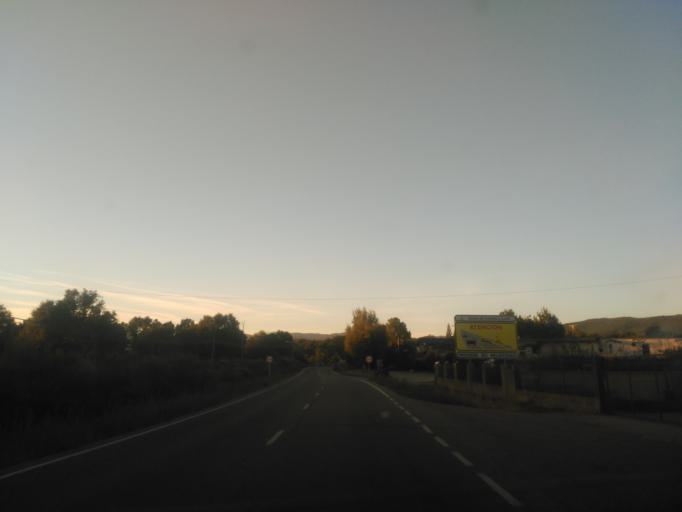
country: ES
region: Castille and Leon
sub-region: Provincia de Zamora
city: Puebla de Sanabria
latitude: 42.0689
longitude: -6.6213
